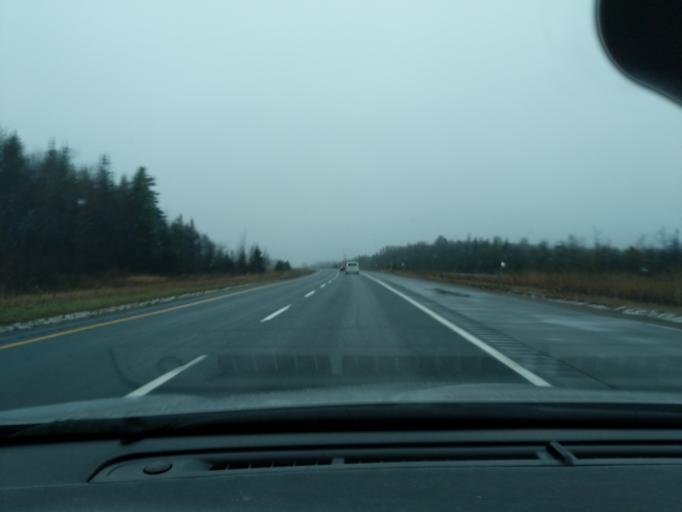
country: CA
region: Quebec
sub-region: Capitale-Nationale
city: Neuville
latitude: 46.7423
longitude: -71.5490
